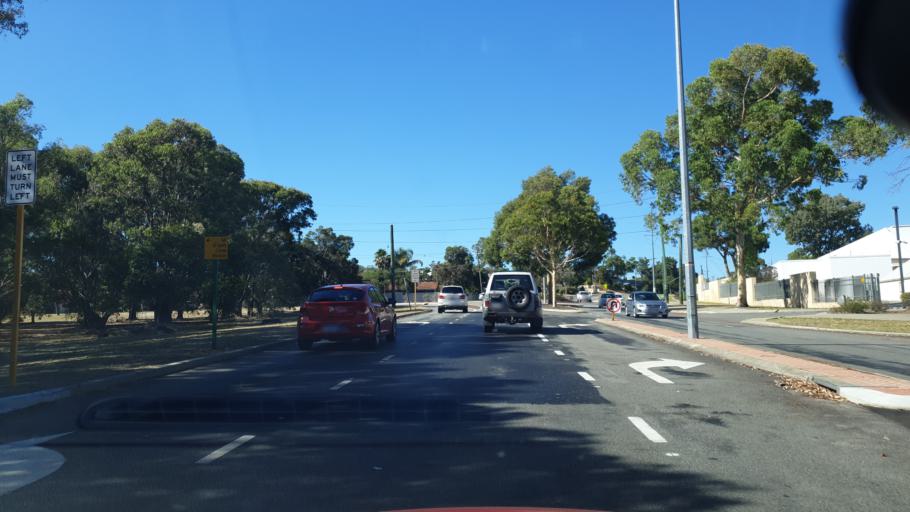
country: AU
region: Western Australia
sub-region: Canning
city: Rossmoyne
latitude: -32.0483
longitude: 115.8598
